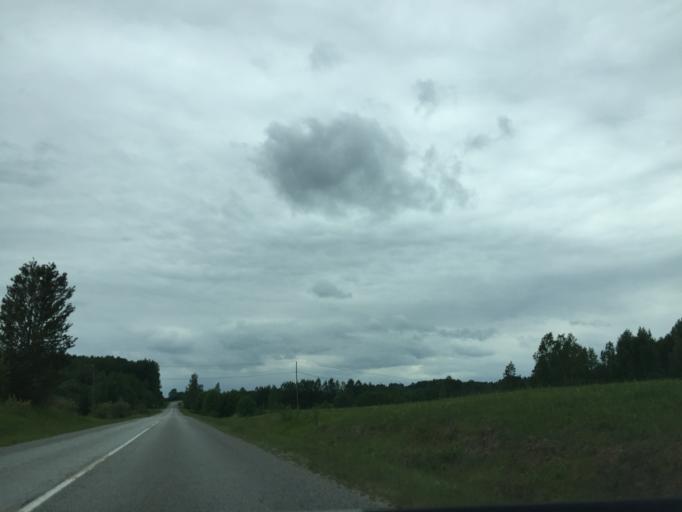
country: LV
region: Aglona
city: Aglona
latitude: 56.1356
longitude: 27.0794
